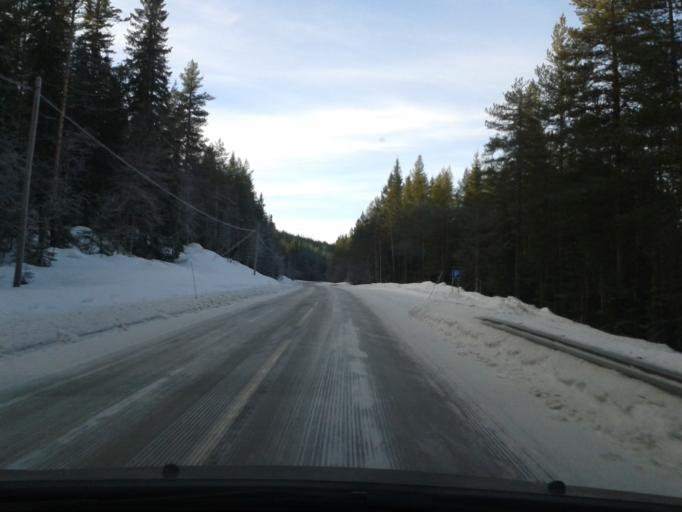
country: SE
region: Vaesternorrland
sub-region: OErnskoeldsviks Kommun
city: Bredbyn
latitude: 63.6619
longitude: 17.8465
